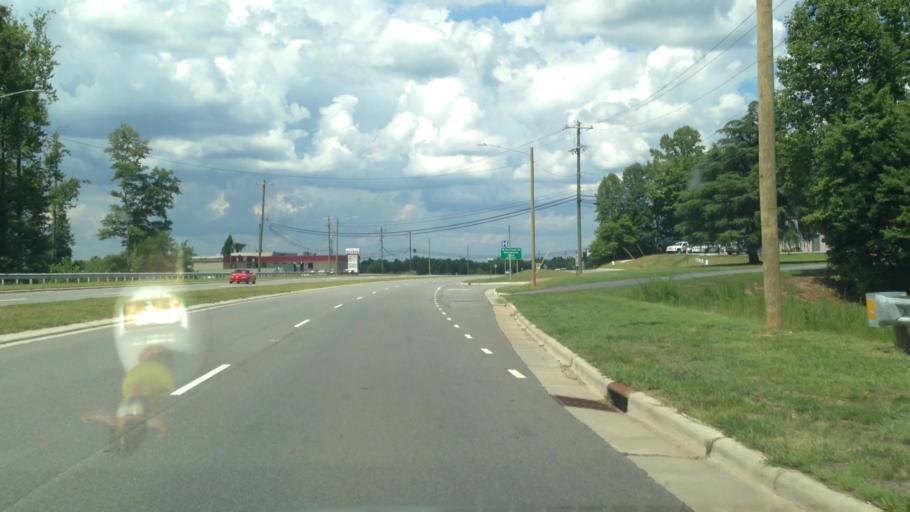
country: US
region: North Carolina
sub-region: Rockingham County
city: Reidsville
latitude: 36.3538
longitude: -79.6924
